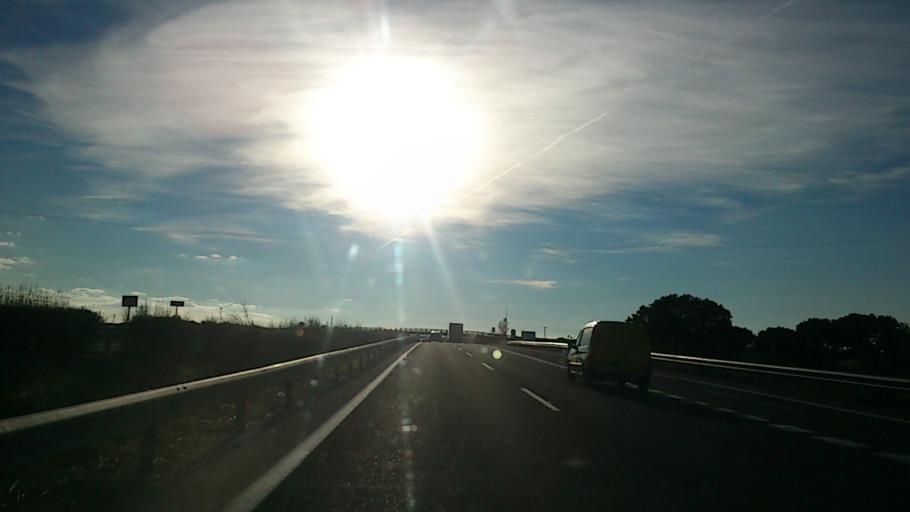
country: ES
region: Castille-La Mancha
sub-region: Provincia de Guadalajara
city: Mirabueno
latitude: 40.9327
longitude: -2.7106
